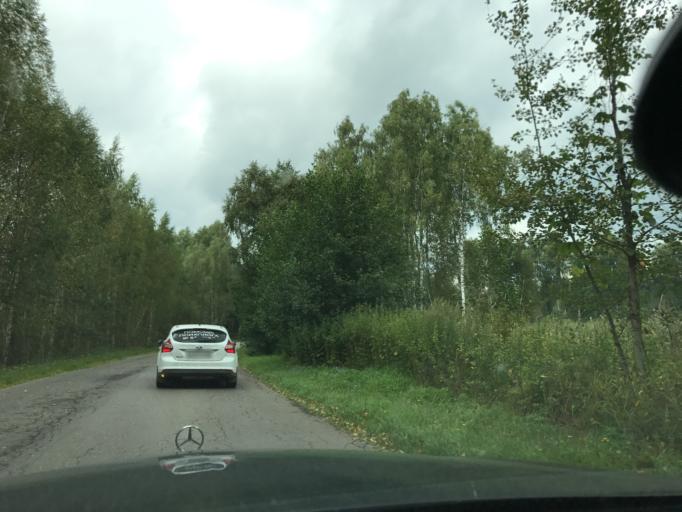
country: RU
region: Vladimir
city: Galitsy
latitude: 55.9974
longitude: 42.8430
